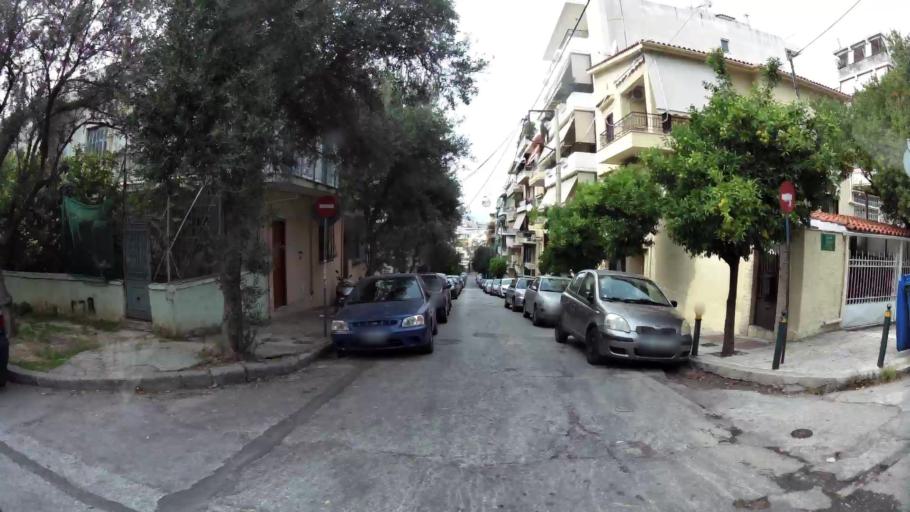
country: GR
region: Attica
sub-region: Nomarchia Athinas
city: Nea Ionia
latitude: 38.0367
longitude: 23.7520
